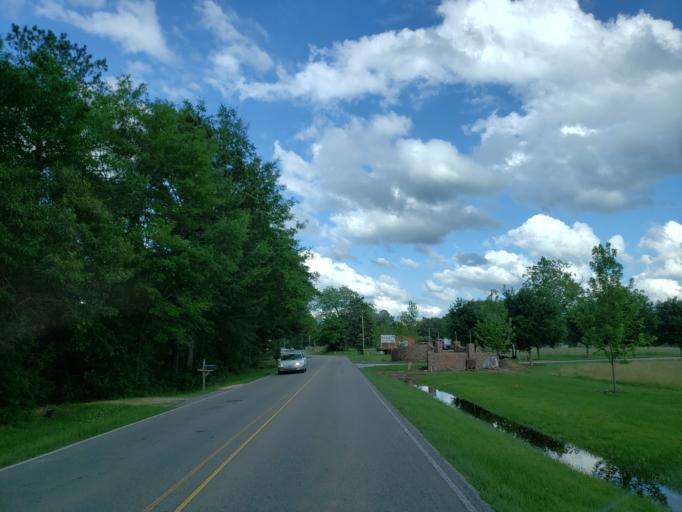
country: US
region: Mississippi
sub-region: Forrest County
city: Petal
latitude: 31.3103
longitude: -89.2179
